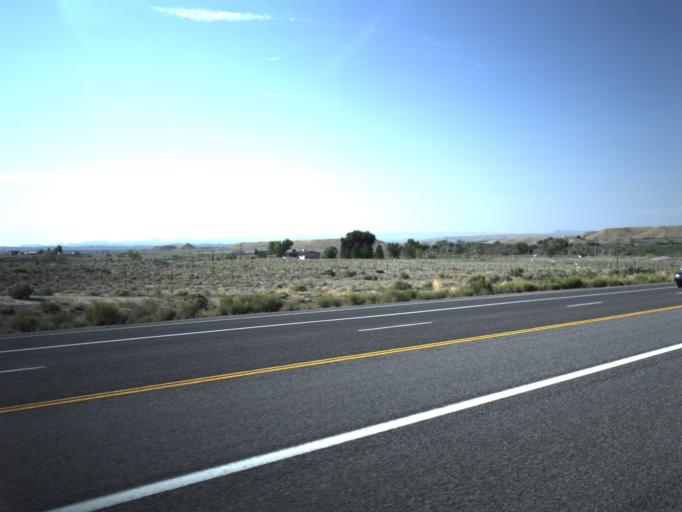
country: US
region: Utah
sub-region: Emery County
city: Huntington
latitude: 39.3598
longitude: -110.9267
